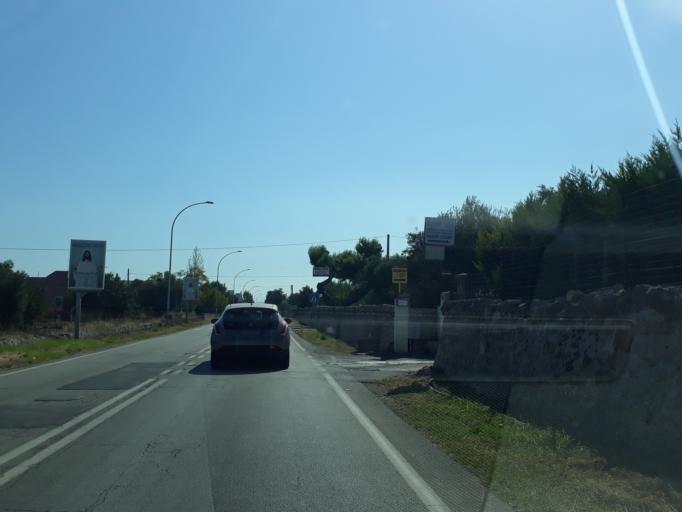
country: IT
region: Apulia
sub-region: Provincia di Bari
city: Monopoli
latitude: 40.9347
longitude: 17.3098
